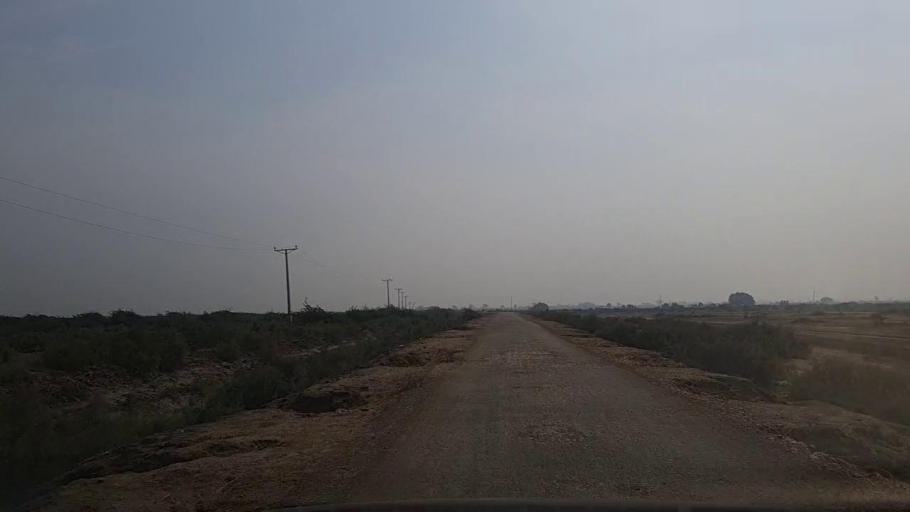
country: PK
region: Sindh
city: Mirpur Sakro
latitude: 24.3876
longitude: 67.7524
